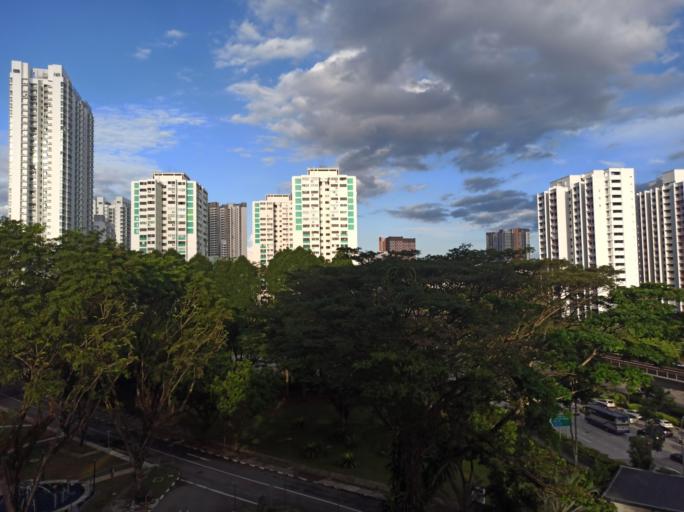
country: SG
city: Singapore
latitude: 1.3118
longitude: 103.7732
